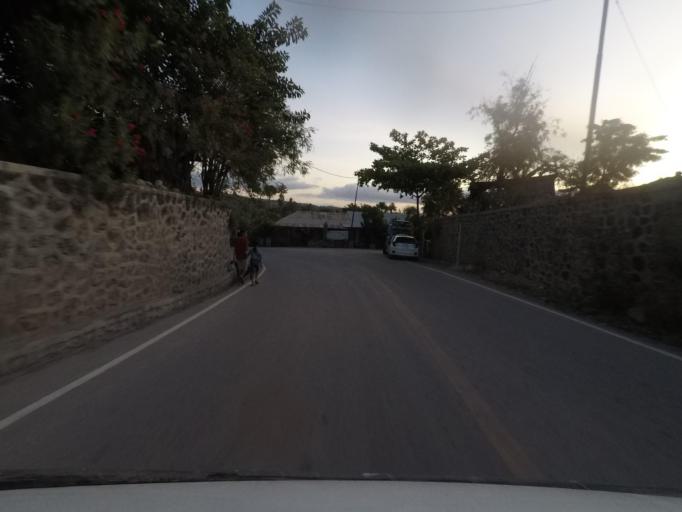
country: TL
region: Baucau
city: Baucau
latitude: -8.4742
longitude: 126.5959
